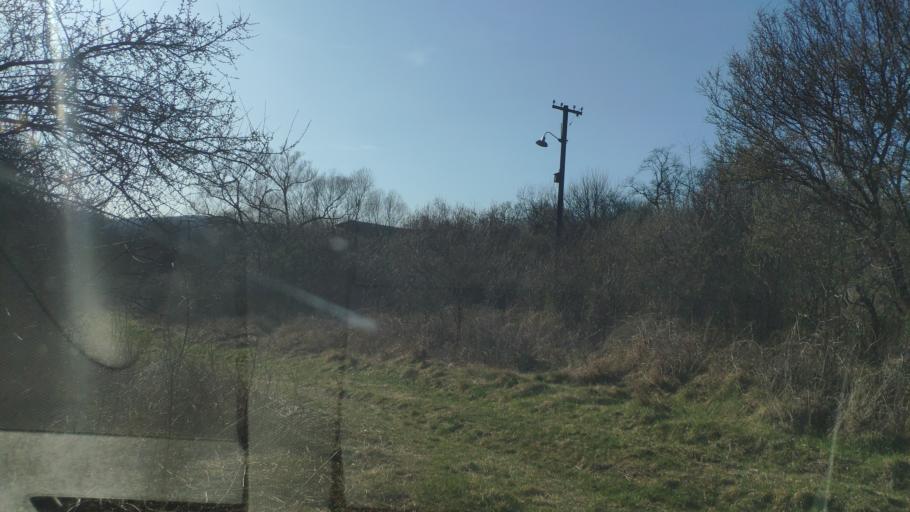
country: SK
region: Banskobystricky
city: Revuca
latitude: 48.5422
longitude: 20.2442
